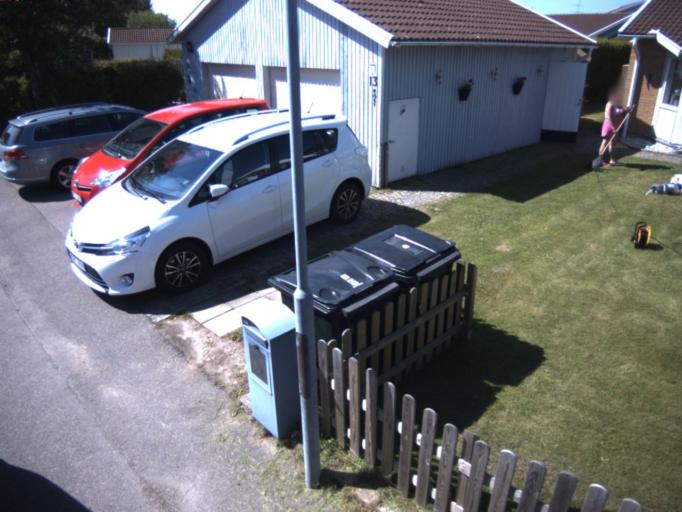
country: SE
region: Skane
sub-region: Helsingborg
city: Gantofta
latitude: 55.9842
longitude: 12.8035
